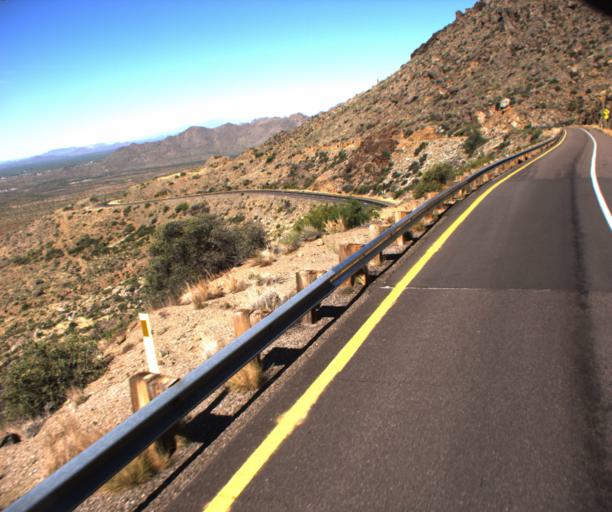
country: US
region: Arizona
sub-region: Yavapai County
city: Congress
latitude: 34.2059
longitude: -112.7821
